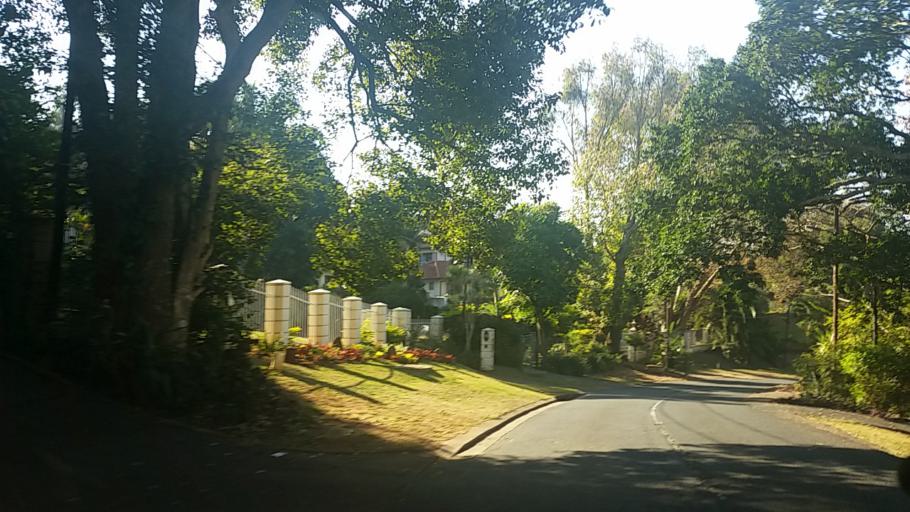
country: ZA
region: KwaZulu-Natal
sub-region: eThekwini Metropolitan Municipality
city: Berea
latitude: -29.8443
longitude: 30.9134
